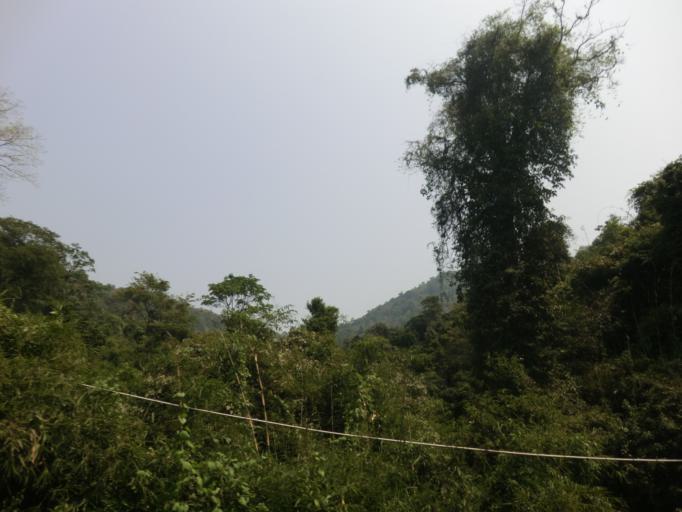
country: VN
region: Lam Dong
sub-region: Thanh Pho Bao Loc
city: Bao Loc
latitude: 11.4342
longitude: 107.6981
